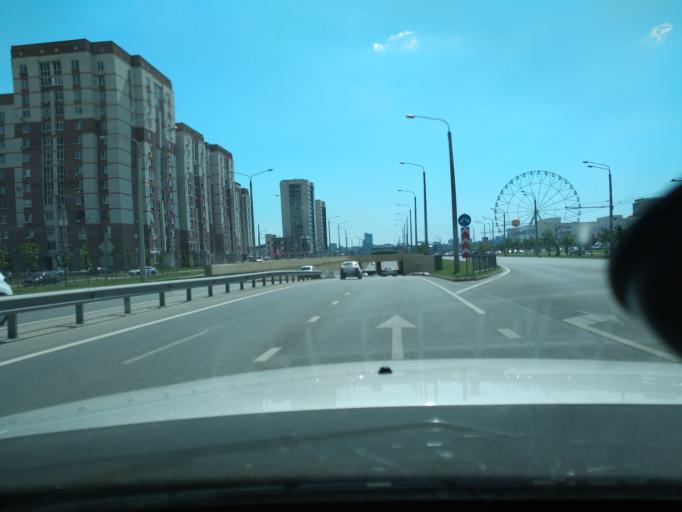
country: RU
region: Tatarstan
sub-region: Gorod Kazan'
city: Kazan
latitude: 55.8181
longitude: 49.1336
